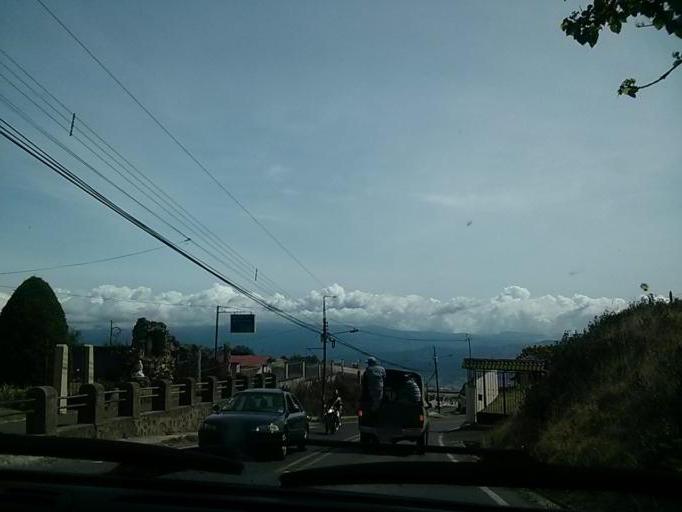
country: CR
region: Cartago
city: Cot
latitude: 9.9199
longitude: -83.8792
